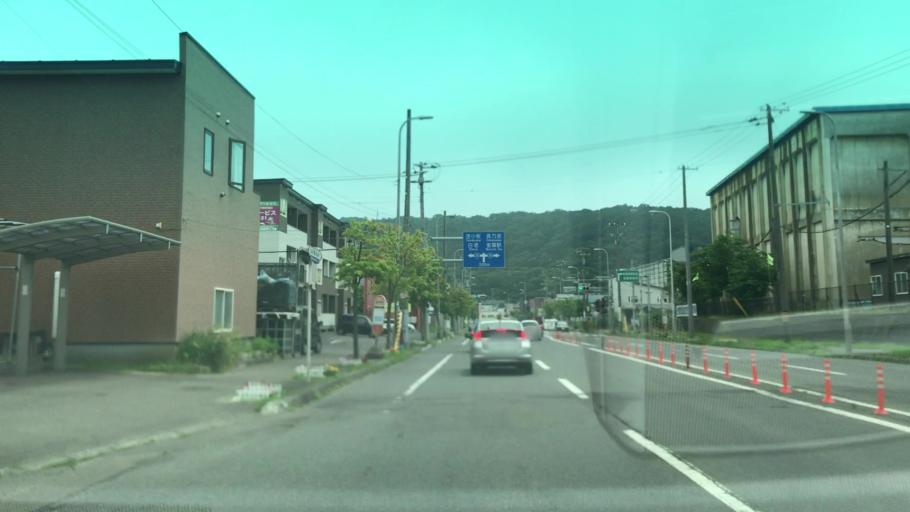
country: JP
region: Hokkaido
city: Muroran
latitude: 42.3582
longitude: 141.0445
